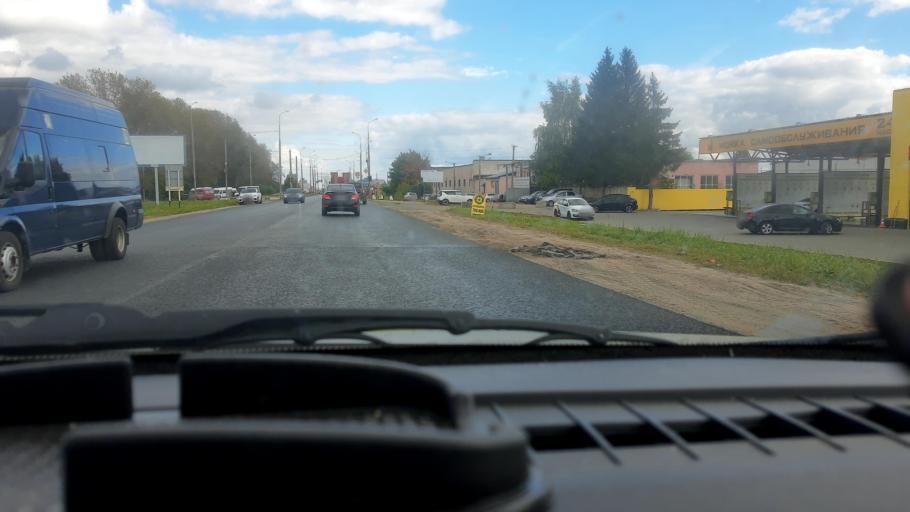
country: RU
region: Mariy-El
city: Medvedevo
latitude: 56.6378
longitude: 47.7683
